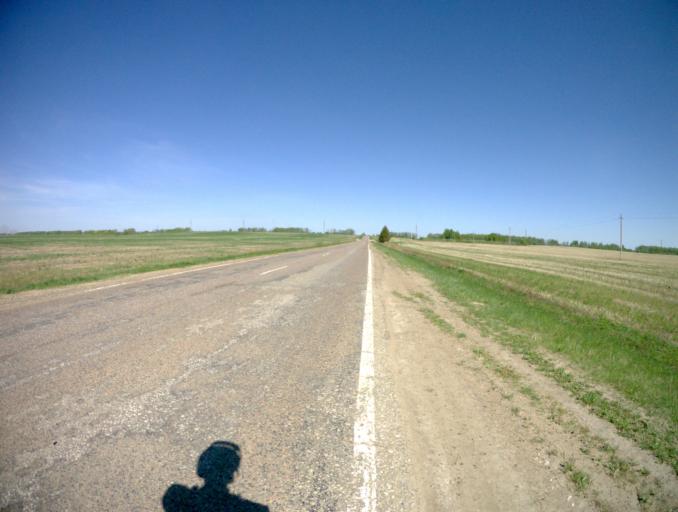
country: RU
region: Vladimir
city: Suzdal'
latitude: 56.3729
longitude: 40.4476
